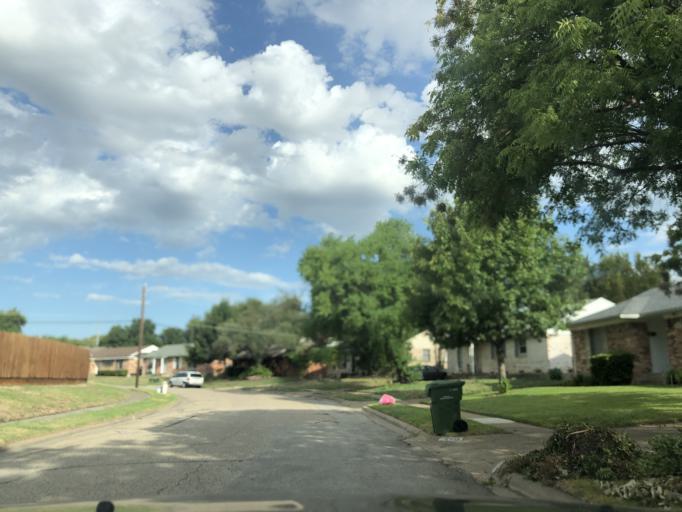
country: US
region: Texas
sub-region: Dallas County
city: Garland
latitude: 32.8865
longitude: -96.6634
